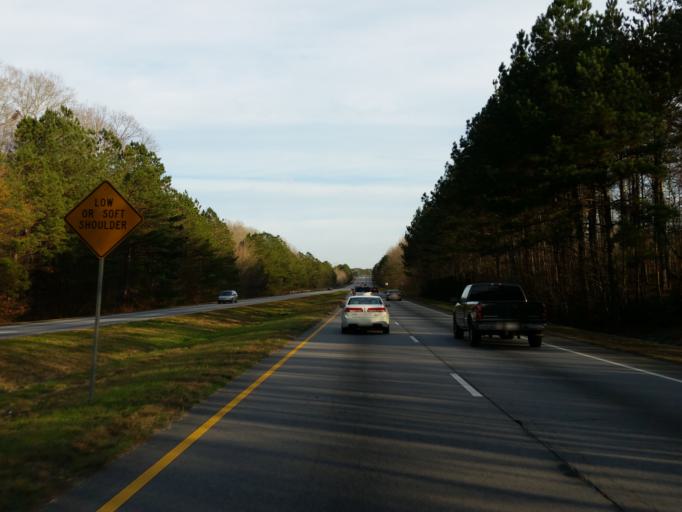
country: US
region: Georgia
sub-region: Cobb County
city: Powder Springs
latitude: 33.8787
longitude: -84.7153
